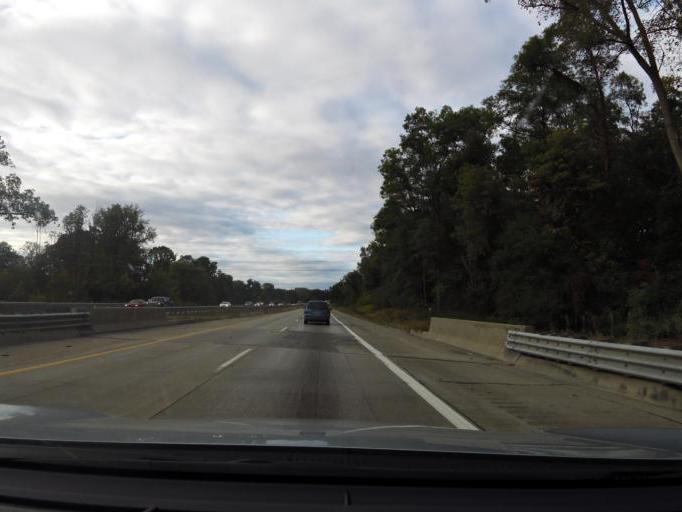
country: US
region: Michigan
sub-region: Livingston County
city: Brighton
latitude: 42.6553
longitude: -83.7574
